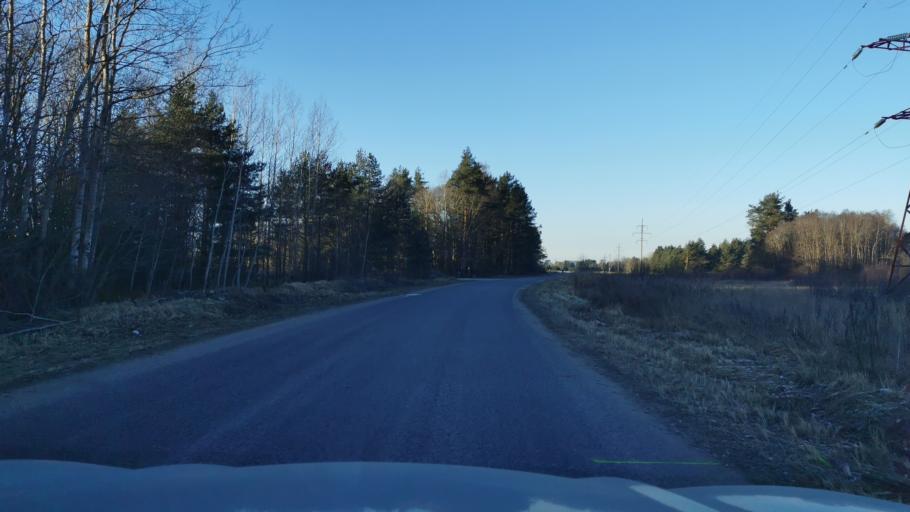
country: EE
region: Ida-Virumaa
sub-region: Puessi linn
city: Pussi
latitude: 59.3400
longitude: 27.0608
